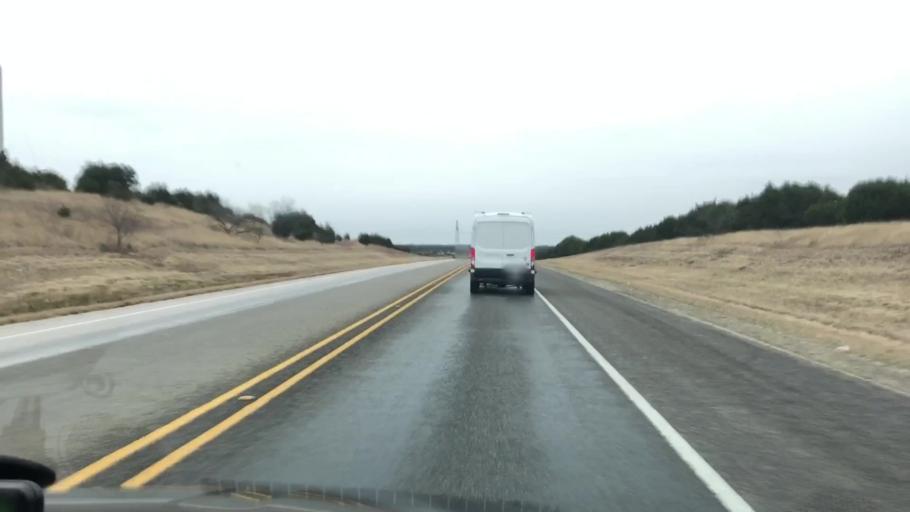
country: US
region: Texas
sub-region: Lampasas County
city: Lampasas
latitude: 31.1333
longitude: -98.1872
